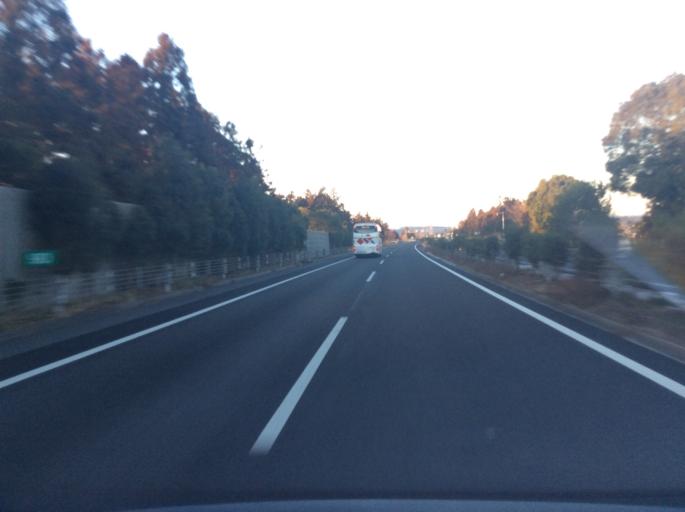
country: JP
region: Ibaraki
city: Mito-shi
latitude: 36.4302
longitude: 140.4454
